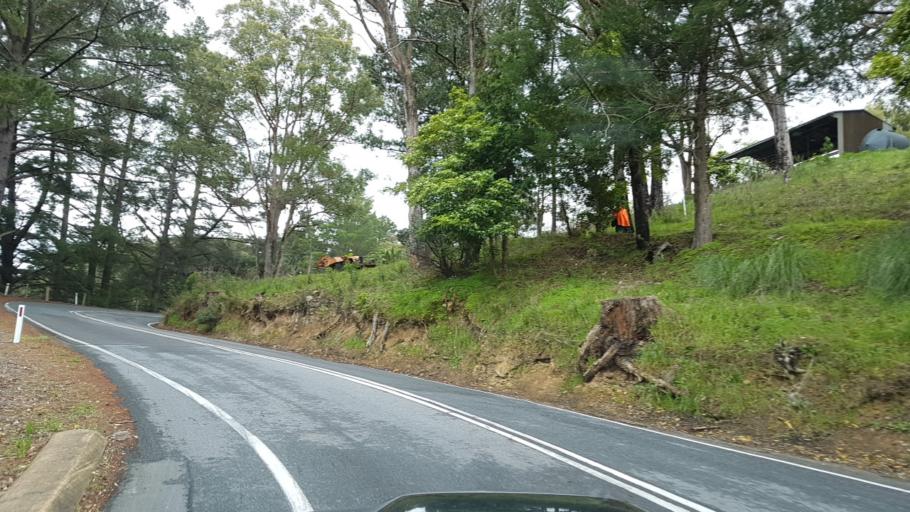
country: AU
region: South Australia
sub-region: Adelaide Hills
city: Bridgewater
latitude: -34.9435
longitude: 138.7717
